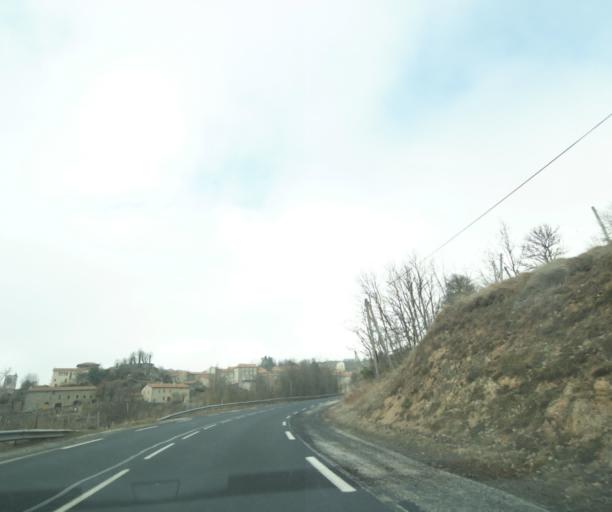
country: FR
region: Languedoc-Roussillon
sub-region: Departement de la Lozere
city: Langogne
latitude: 44.7661
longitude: 3.8851
